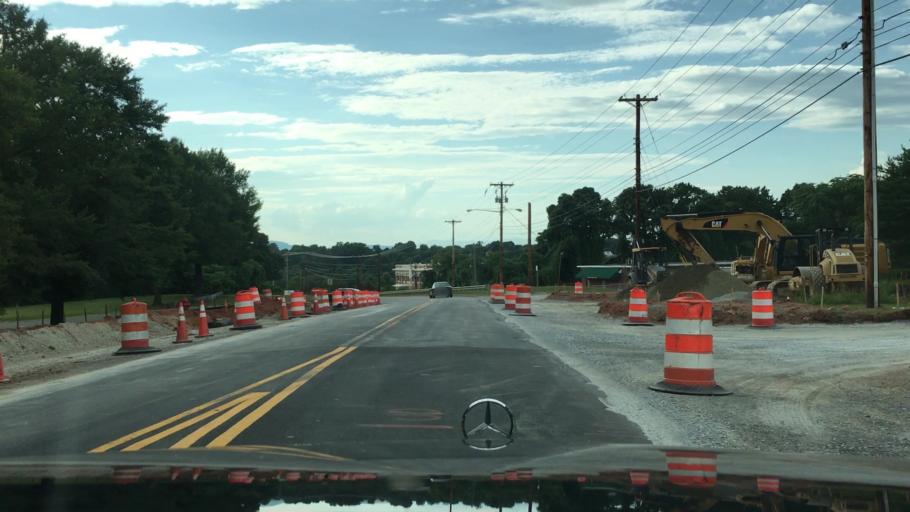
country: US
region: Virginia
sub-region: City of Lynchburg
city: West Lynchburg
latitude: 37.3819
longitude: -79.1611
